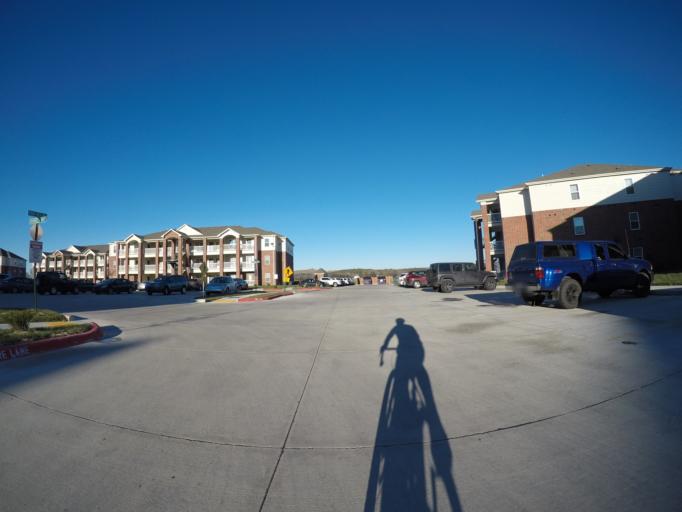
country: US
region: Kansas
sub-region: Riley County
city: Manhattan
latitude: 39.2222
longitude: -96.5639
